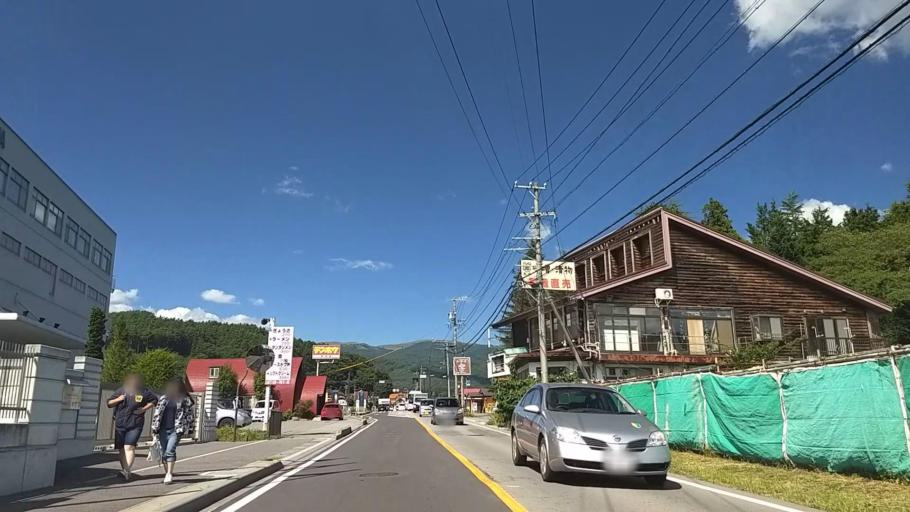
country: JP
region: Nagano
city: Chino
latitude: 36.0130
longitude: 138.1757
